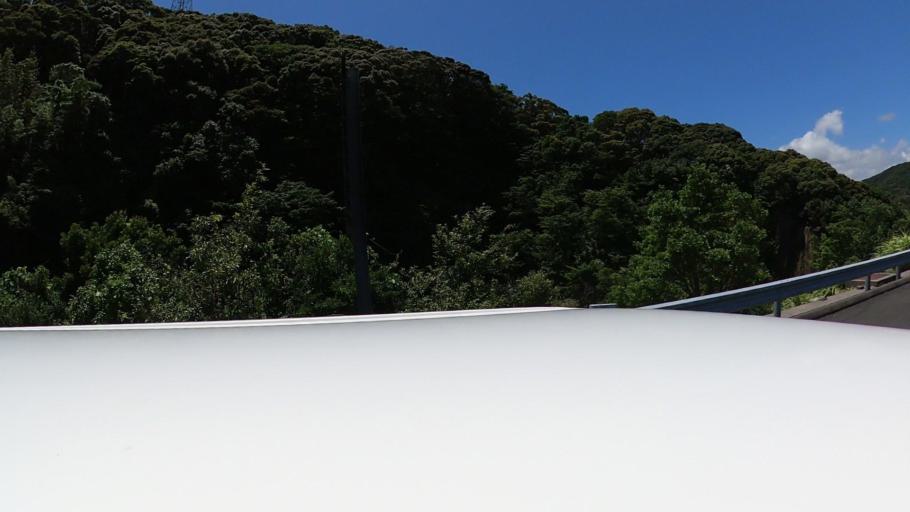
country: JP
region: Miyazaki
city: Nobeoka
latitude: 32.3958
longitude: 131.6200
